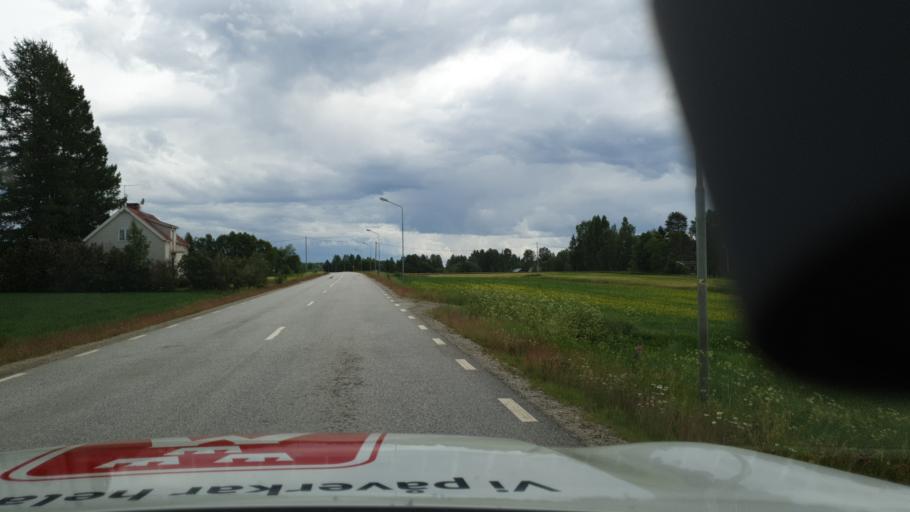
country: SE
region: Vaesterbotten
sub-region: Vindelns Kommun
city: Vindeln
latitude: 64.1705
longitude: 19.4891
